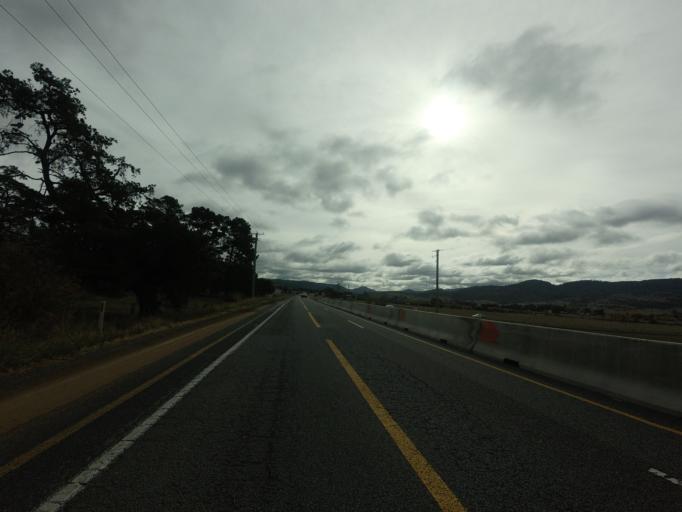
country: AU
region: Tasmania
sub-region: Brighton
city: Bridgewater
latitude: -42.6623
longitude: 147.2483
